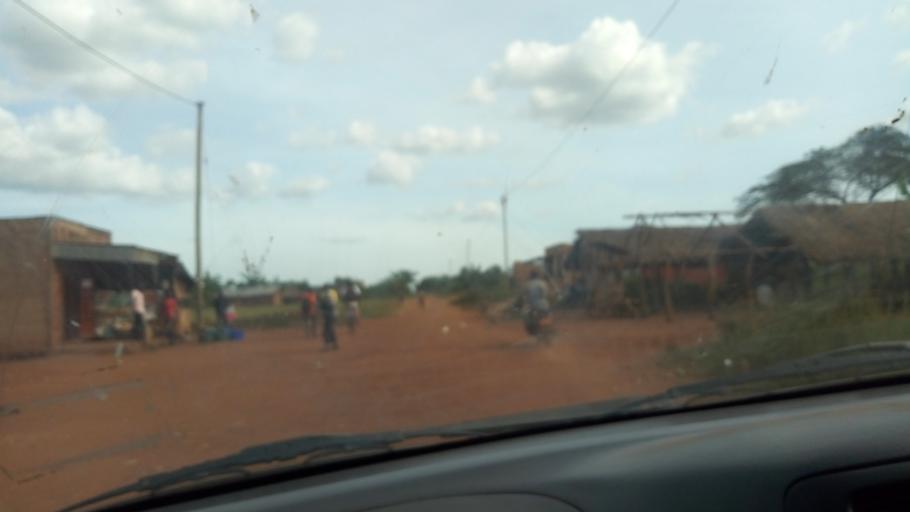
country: UG
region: Western Region
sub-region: Kiryandongo District
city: Kiryandongo
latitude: 1.8097
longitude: 31.9426
